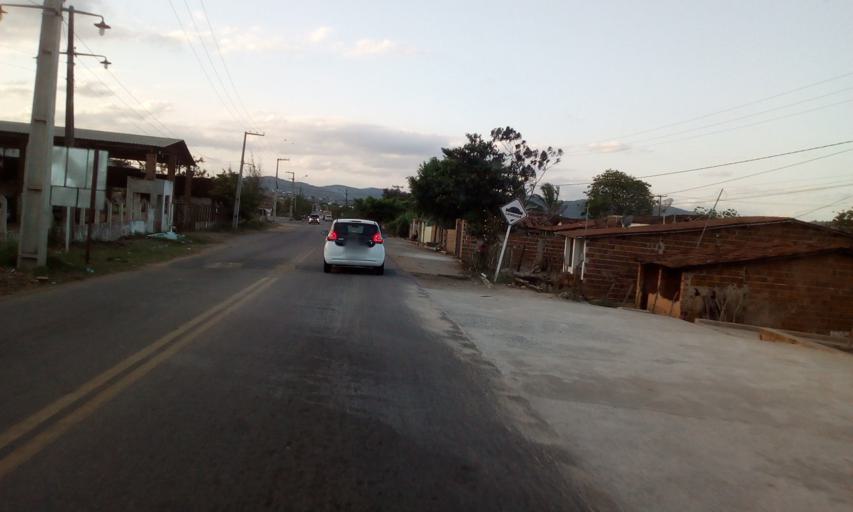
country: BR
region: Paraiba
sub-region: Guarabira
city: Guarabira
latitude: -6.8887
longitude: -35.4675
